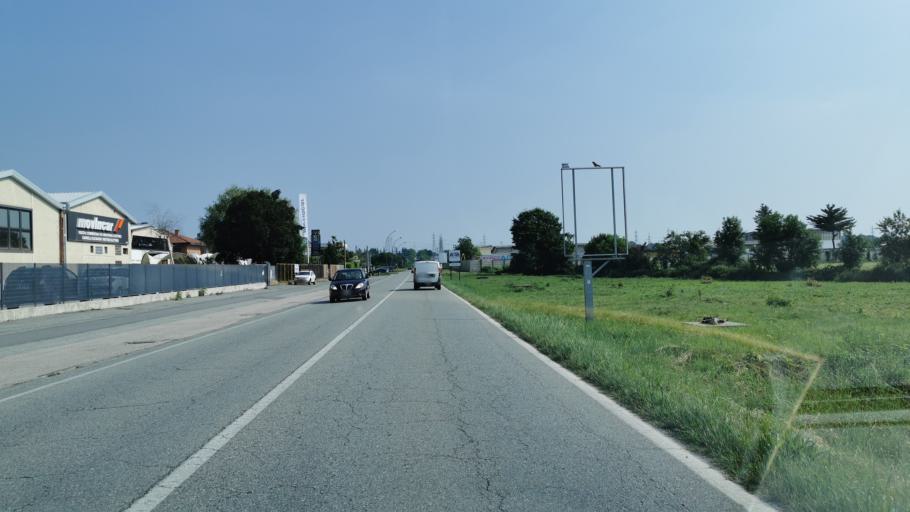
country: IT
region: Piedmont
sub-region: Provincia di Torino
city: Leini
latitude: 45.1990
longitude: 7.7245
